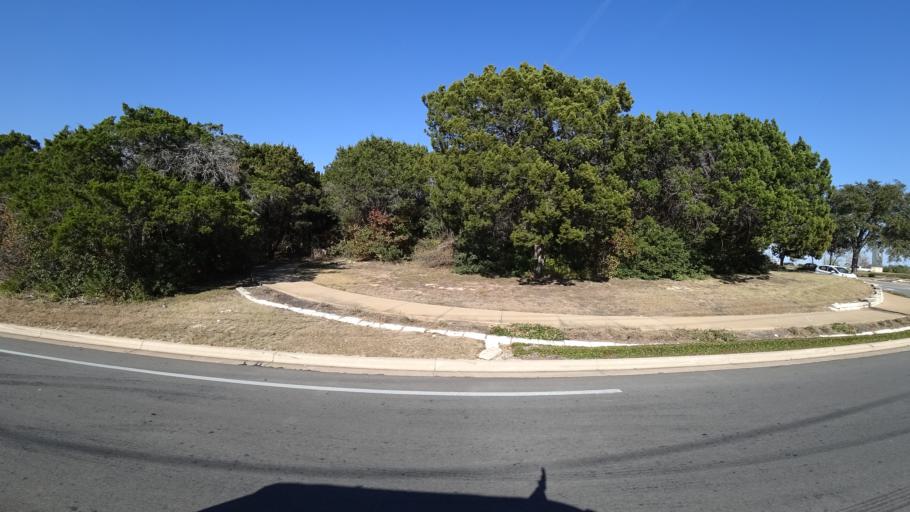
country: US
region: Texas
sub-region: Travis County
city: Hudson Bend
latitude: 30.3935
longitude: -97.8673
